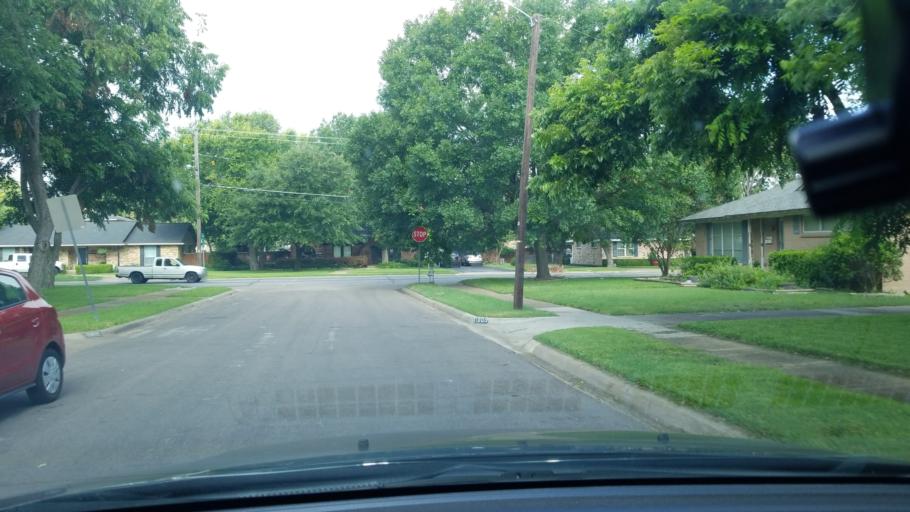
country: US
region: Texas
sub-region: Dallas County
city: Mesquite
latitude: 32.8209
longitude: -96.6839
